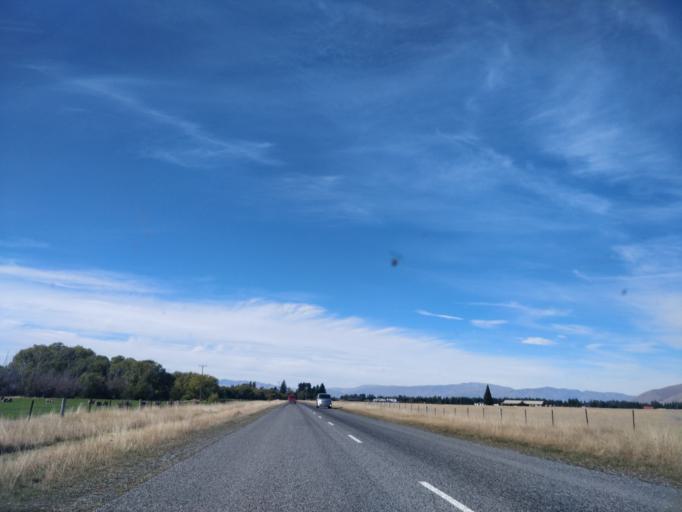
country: NZ
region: Otago
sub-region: Queenstown-Lakes District
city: Wanaka
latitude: -44.2360
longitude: 170.0732
